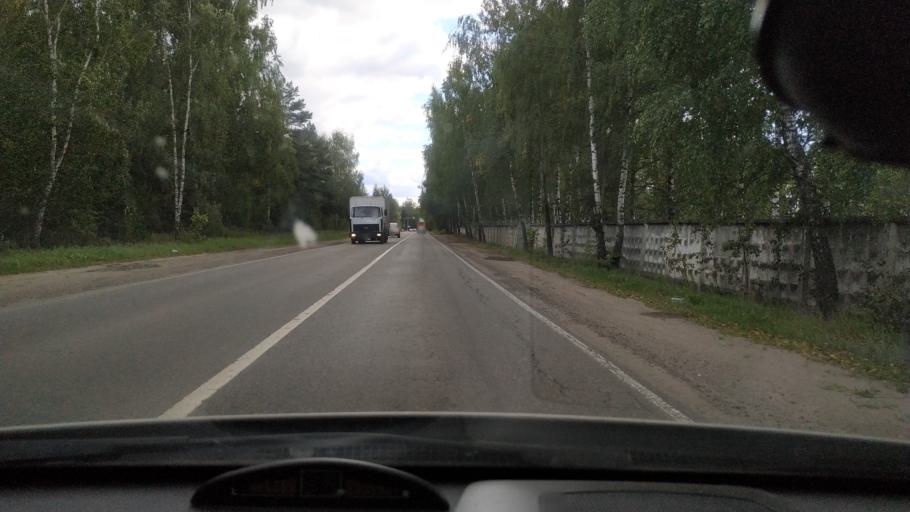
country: RU
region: Moskovskaya
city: Chornaya
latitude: 55.7631
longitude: 38.0736
